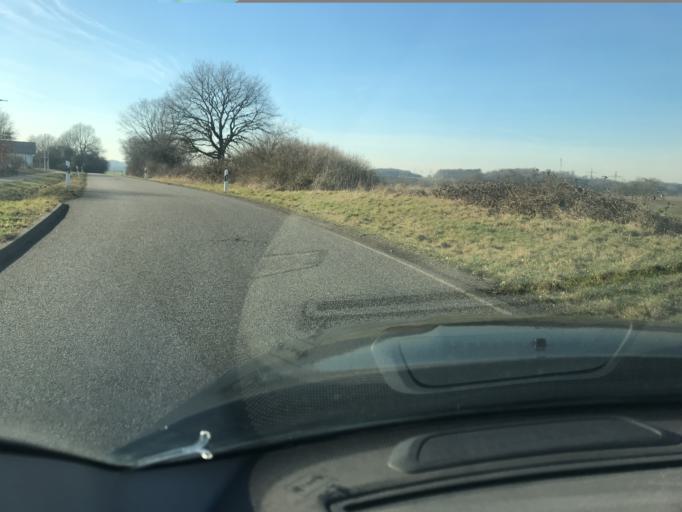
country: DE
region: Rheinland-Pfalz
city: Hundsangen
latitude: 50.4418
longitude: 7.9945
